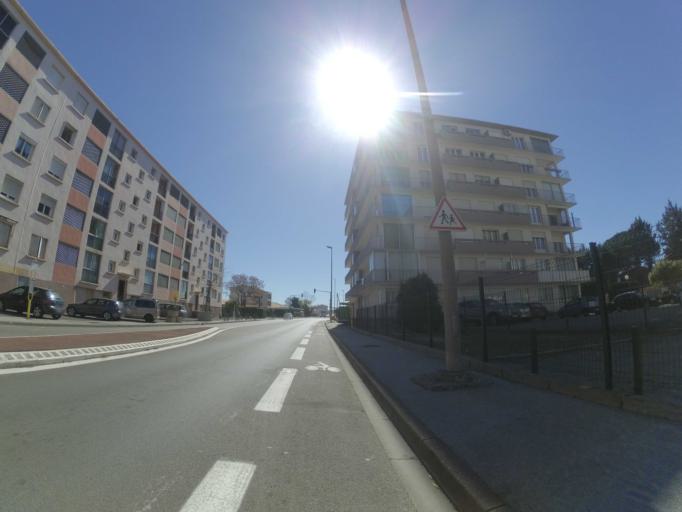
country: FR
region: Languedoc-Roussillon
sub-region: Departement des Pyrenees-Orientales
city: Perpignan
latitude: 42.7097
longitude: 2.8980
